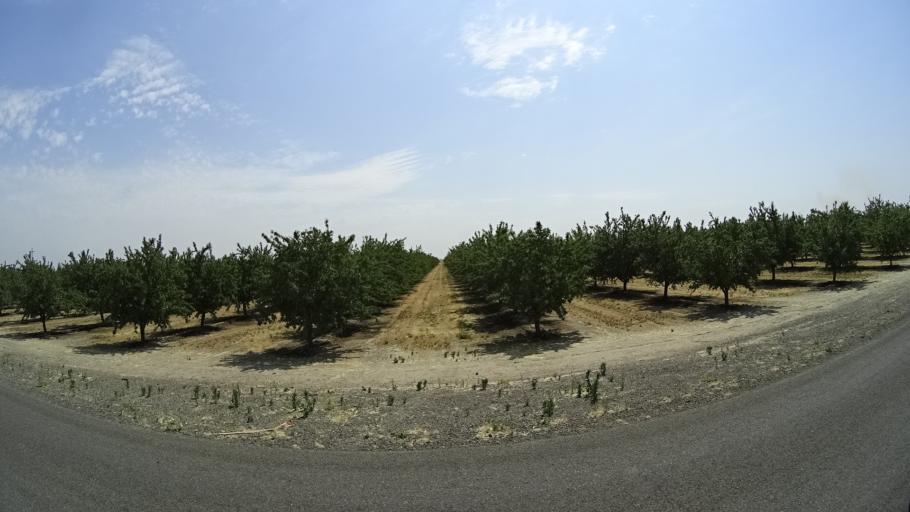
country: US
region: California
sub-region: Fresno County
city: Laton
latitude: 36.3897
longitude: -119.7450
